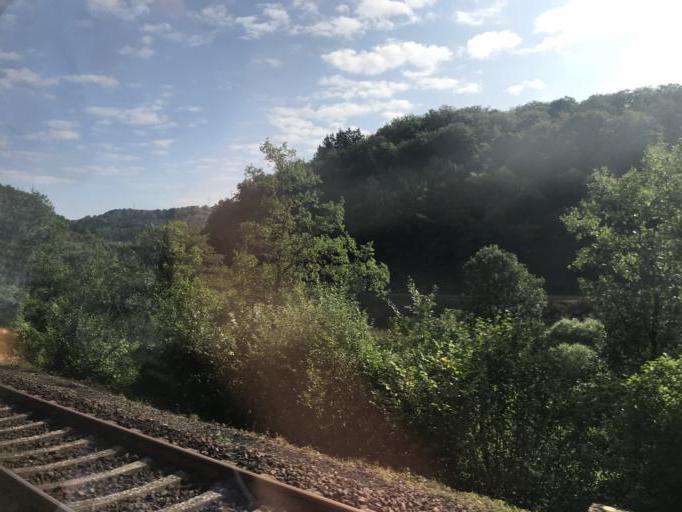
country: DE
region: Rheinland-Pfalz
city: Frauenberg
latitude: 49.6770
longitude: 7.2839
